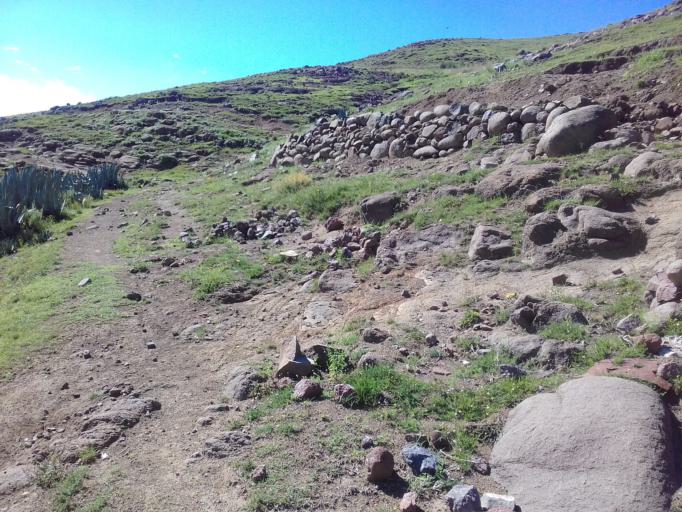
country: LS
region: Thaba-Tseka
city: Thaba-Tseka
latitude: -29.5254
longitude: 28.5816
